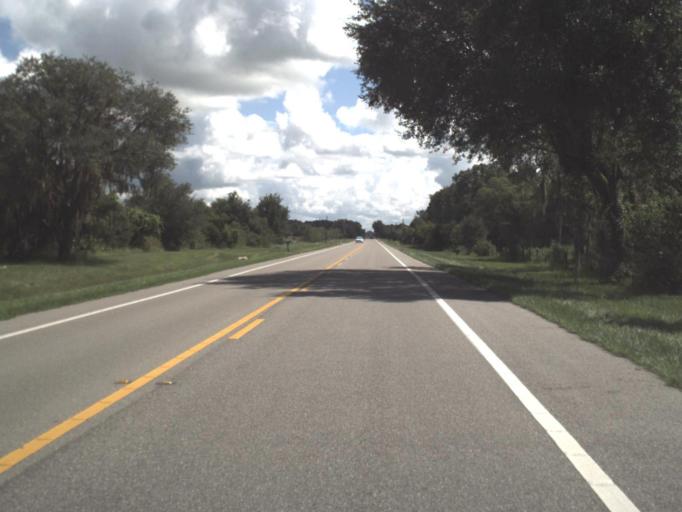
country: US
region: Florida
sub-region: Sarasota County
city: Lake Sarasota
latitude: 27.3627
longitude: -82.2011
